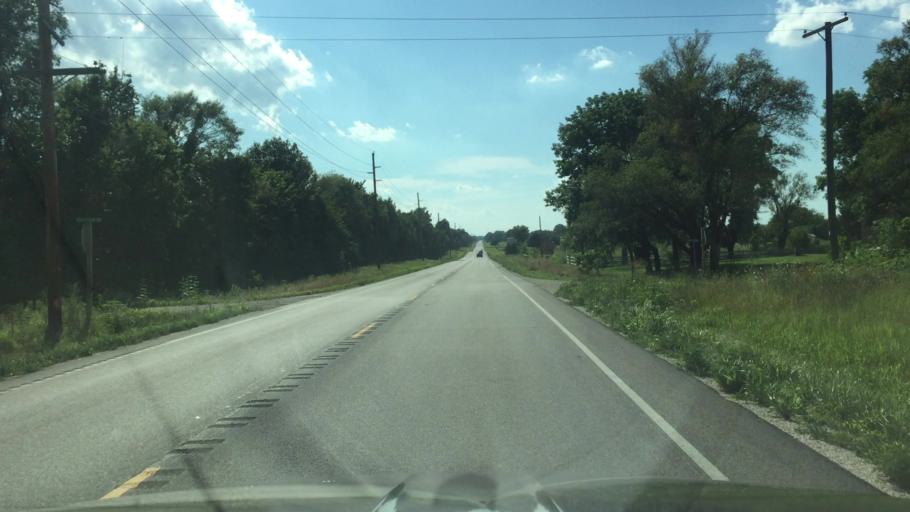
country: US
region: Missouri
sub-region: Morgan County
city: Versailles
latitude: 38.3942
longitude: -92.7157
